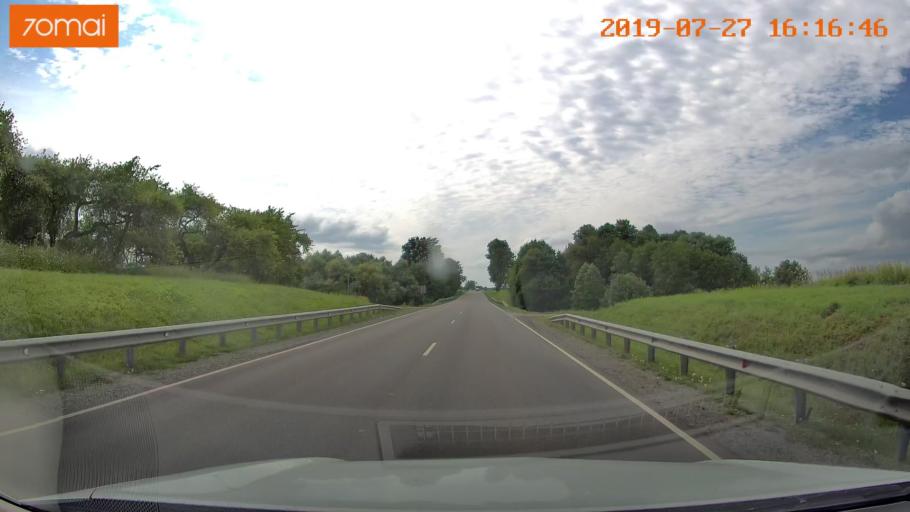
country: RU
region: Kaliningrad
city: Chernyakhovsk
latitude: 54.6237
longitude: 21.5654
